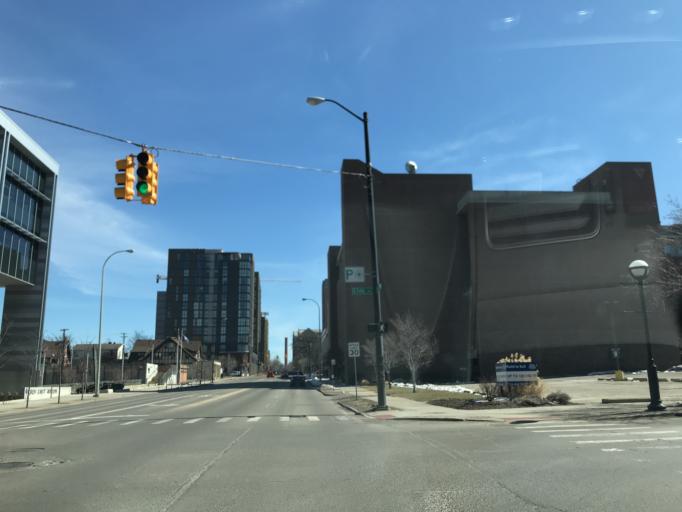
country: US
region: Michigan
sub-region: Washtenaw County
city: Ann Arbor
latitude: 42.2813
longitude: -83.7463
